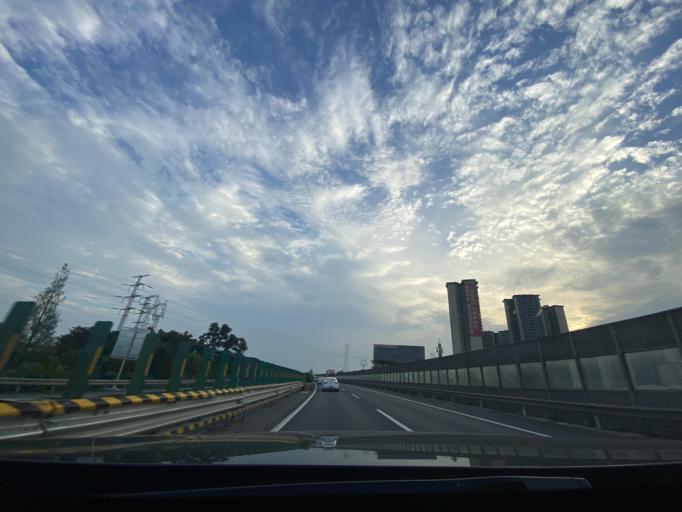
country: CN
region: Sichuan
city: Deyang
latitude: 31.0812
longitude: 104.3864
